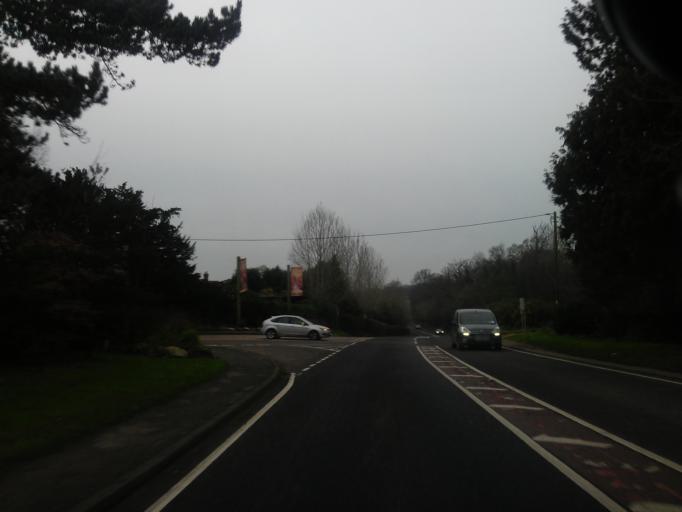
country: GB
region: England
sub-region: Essex
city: Layer de la Haye
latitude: 51.8643
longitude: 0.8361
